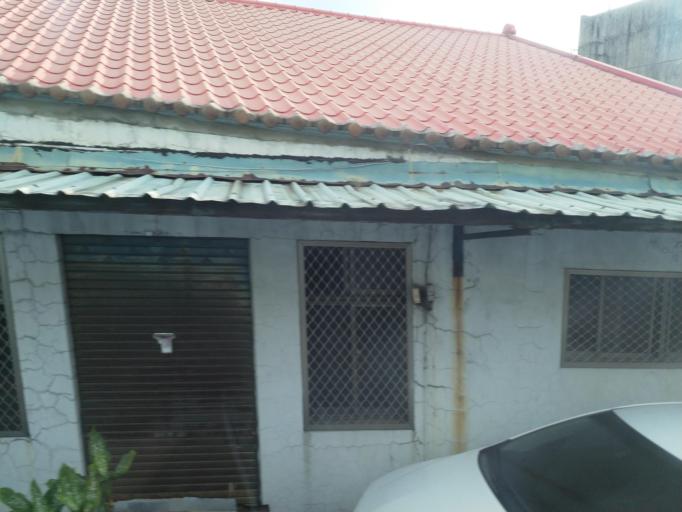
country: TW
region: Taiwan
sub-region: Pingtung
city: Pingtung
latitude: 22.8862
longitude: 120.5329
